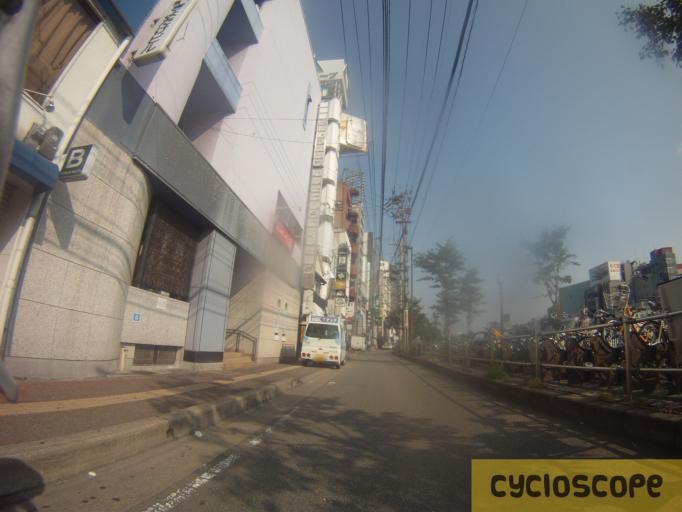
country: JP
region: Fukuoka
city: Fukuoka-shi
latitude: 33.5899
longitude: 130.4070
